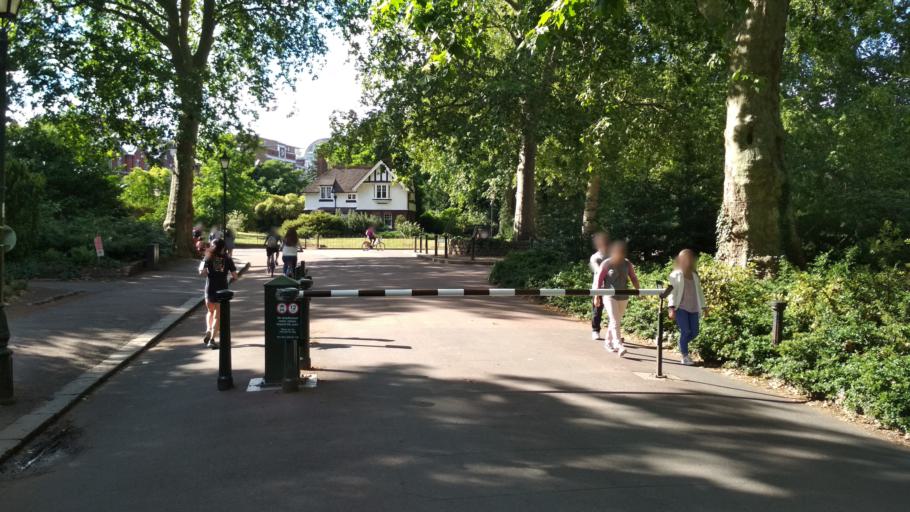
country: GB
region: England
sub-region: Greater London
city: Chelsea
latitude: 51.4792
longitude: -0.1645
